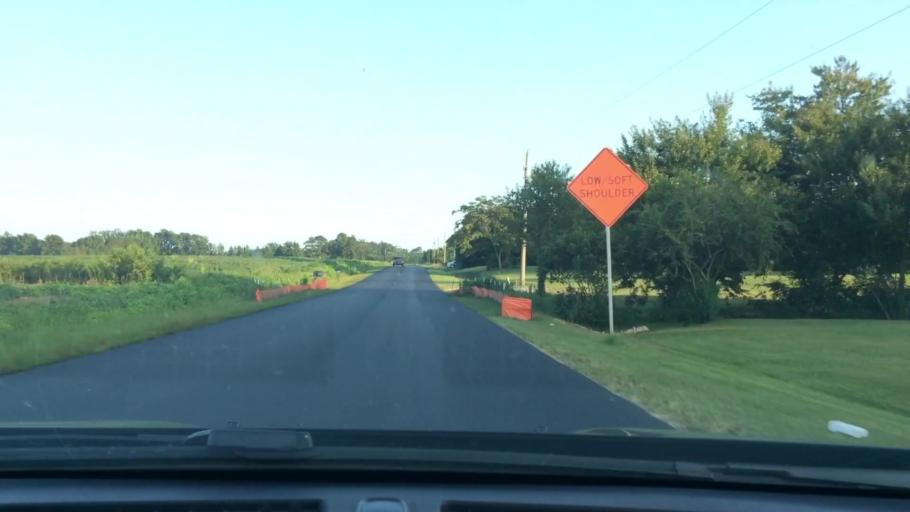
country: US
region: North Carolina
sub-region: Pitt County
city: Ayden
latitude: 35.4575
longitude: -77.4697
